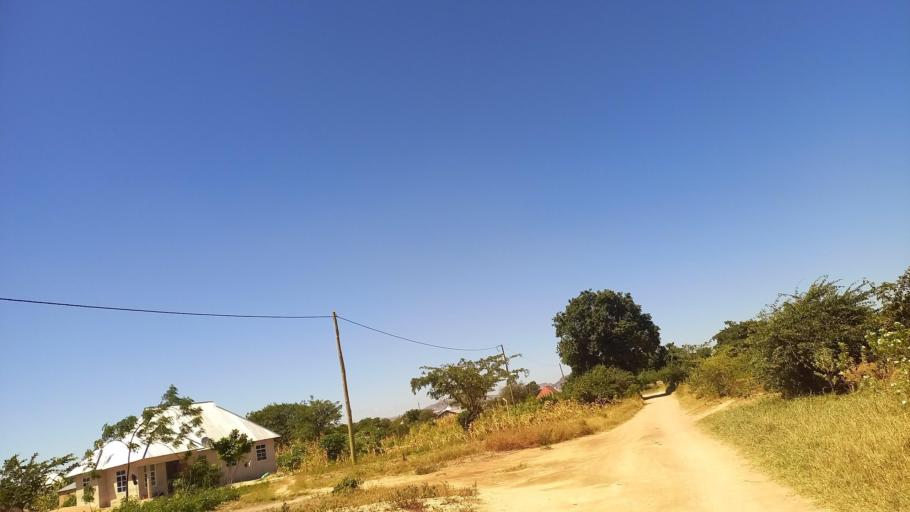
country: TZ
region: Dodoma
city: Dodoma
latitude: -6.1122
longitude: 35.6956
